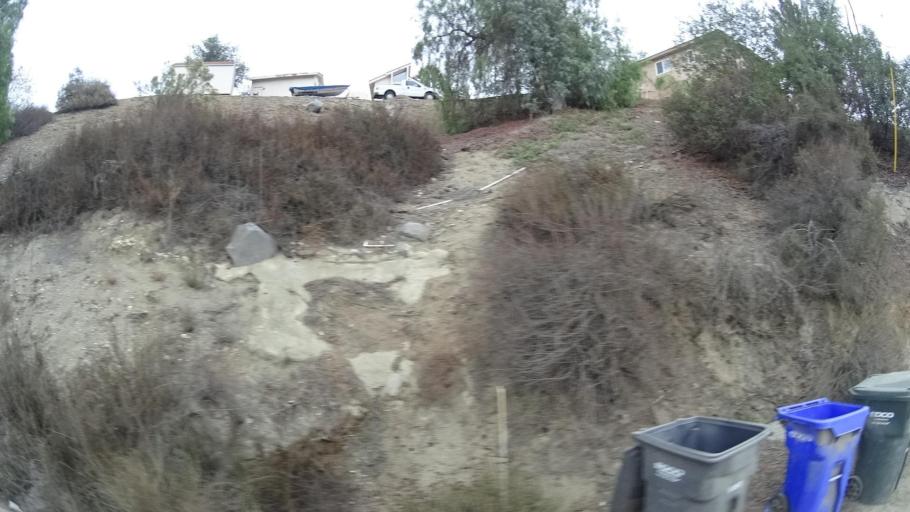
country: US
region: California
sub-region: San Diego County
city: Harbison Canyon
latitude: 32.8202
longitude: -116.8263
